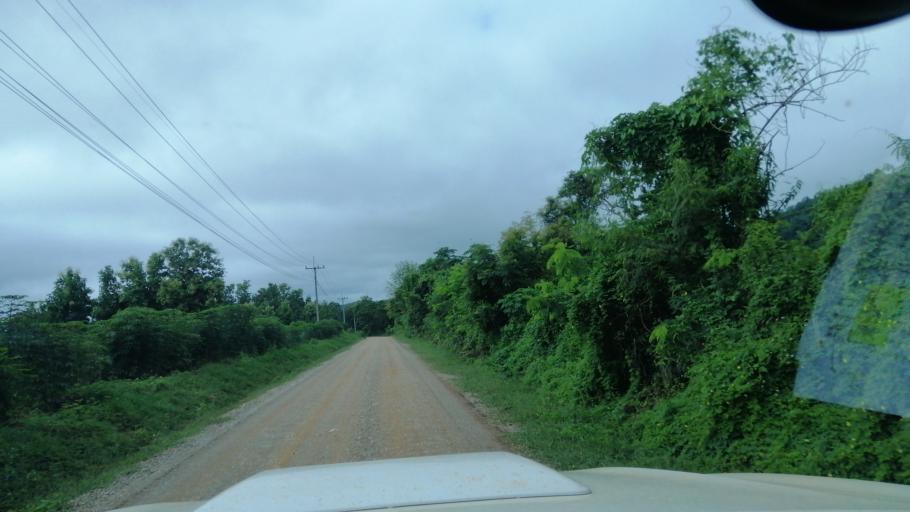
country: LA
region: Xiagnabouli
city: Muang Kenthao
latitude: 17.9727
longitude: 101.4132
